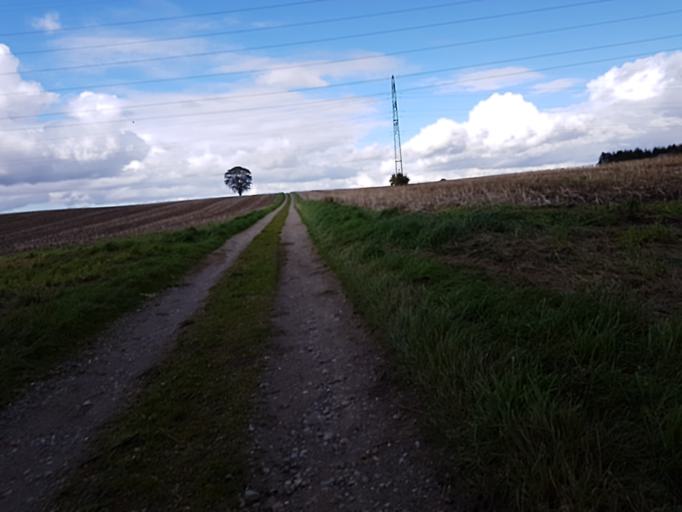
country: DK
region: Capital Region
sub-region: Egedal Kommune
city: Stenlose
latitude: 55.7490
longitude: 12.1873
